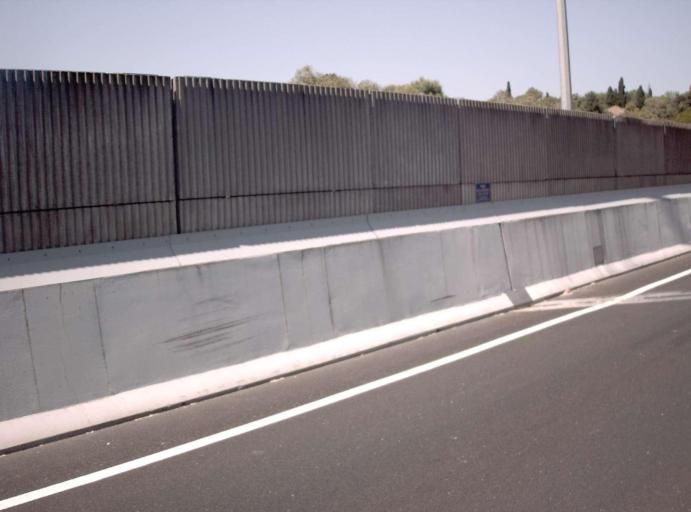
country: AU
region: Victoria
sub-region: Moreland
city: Pascoe Vale
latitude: -37.7358
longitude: 144.9290
